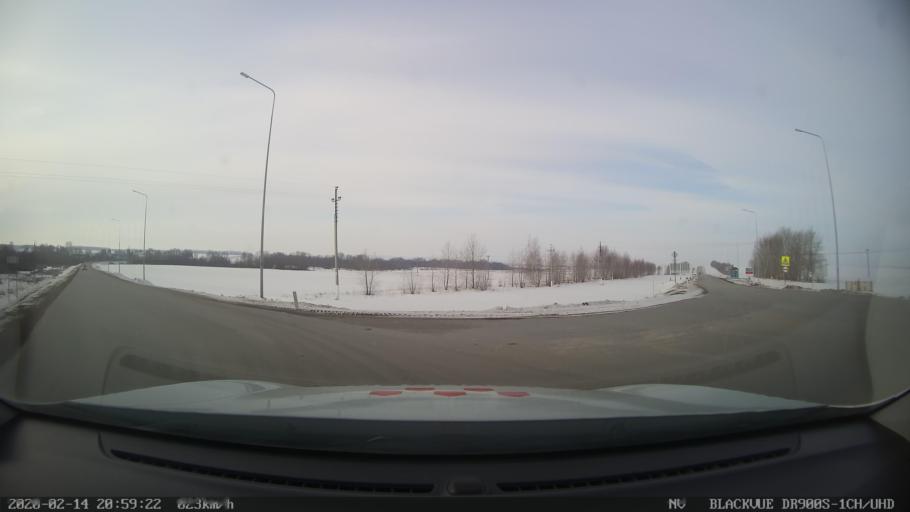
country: RU
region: Tatarstan
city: Kuybyshevskiy Zaton
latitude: 55.1788
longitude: 49.2386
